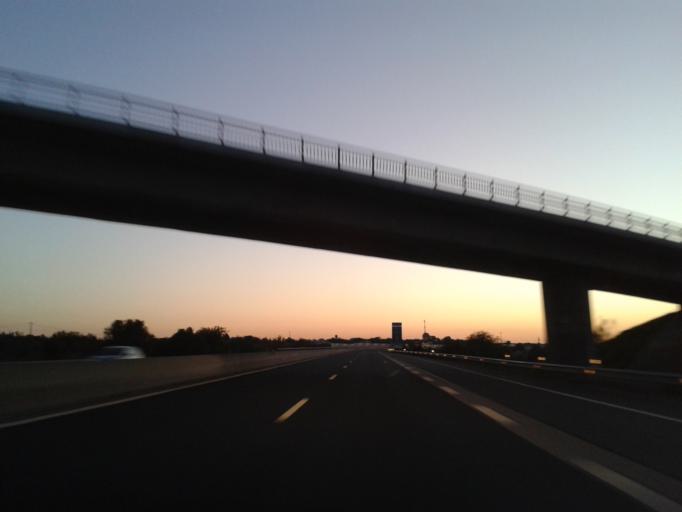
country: PT
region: Faro
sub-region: Albufeira
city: Guia
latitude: 37.1384
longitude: -8.2852
